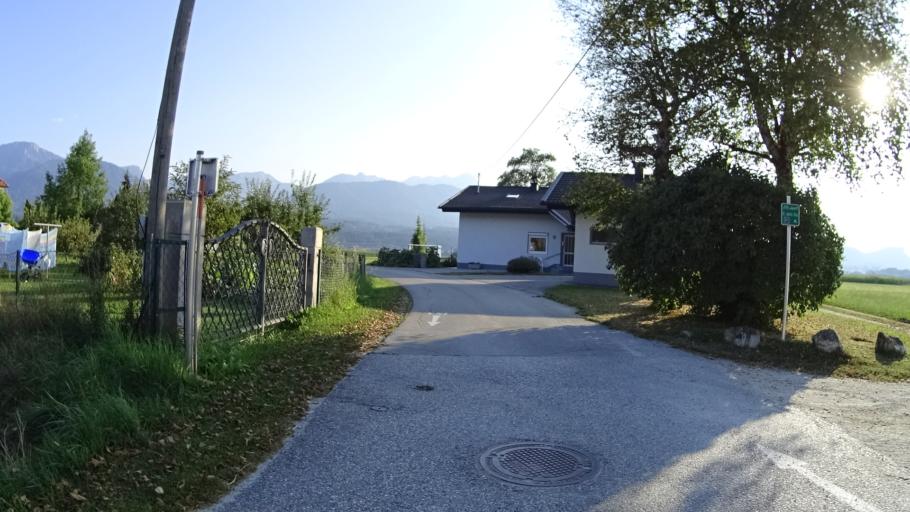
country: AT
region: Carinthia
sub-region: Politischer Bezirk Villach Land
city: Sankt Jakob
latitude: 46.5668
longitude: 14.0571
